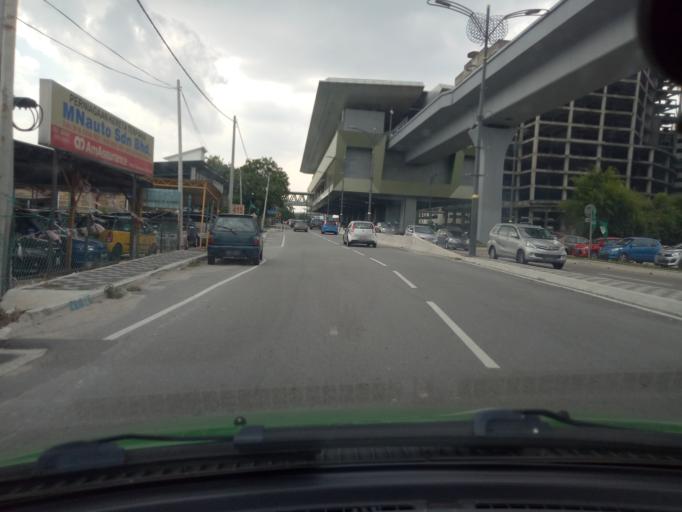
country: MY
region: Selangor
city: Kampong Baharu Balakong
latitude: 2.9996
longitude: 101.7848
